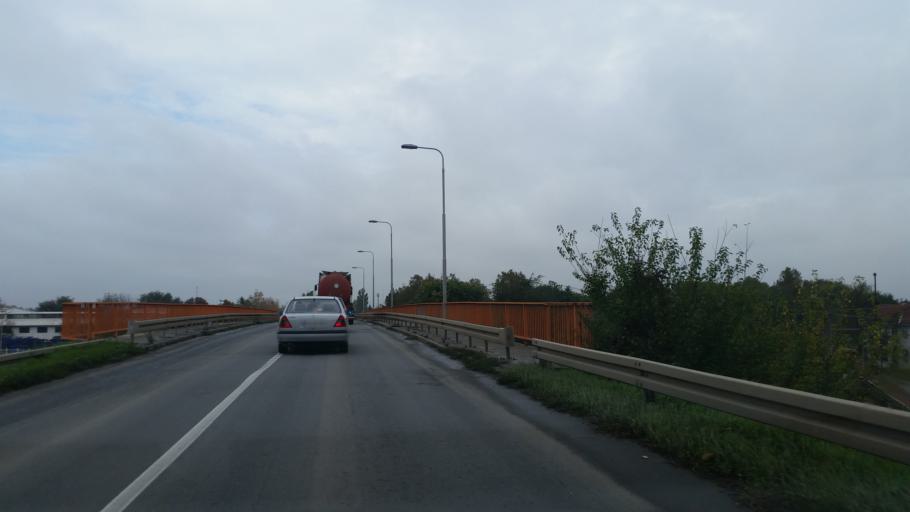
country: RS
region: Autonomna Pokrajina Vojvodina
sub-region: Srednjebanatski Okrug
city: Zrenjanin
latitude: 45.3700
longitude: 20.4201
